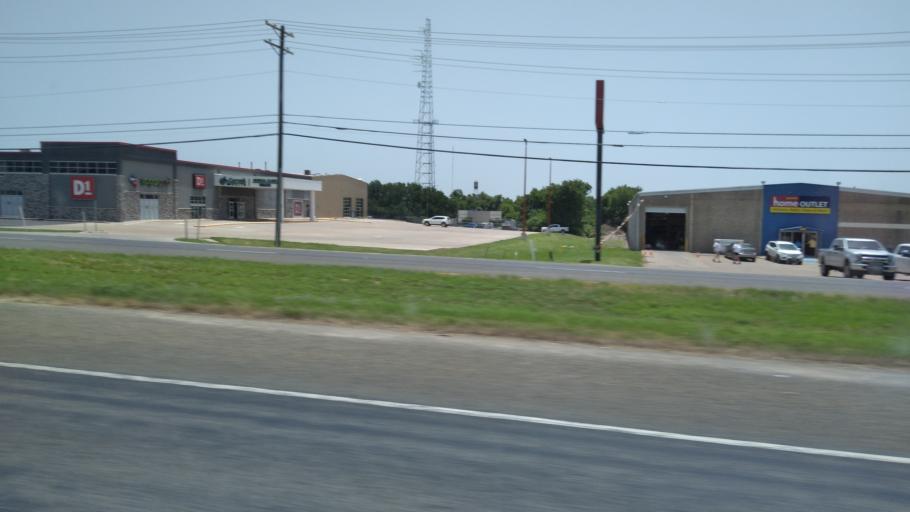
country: US
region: Texas
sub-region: McLennan County
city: Beverly Hills
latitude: 31.5180
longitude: -97.1783
